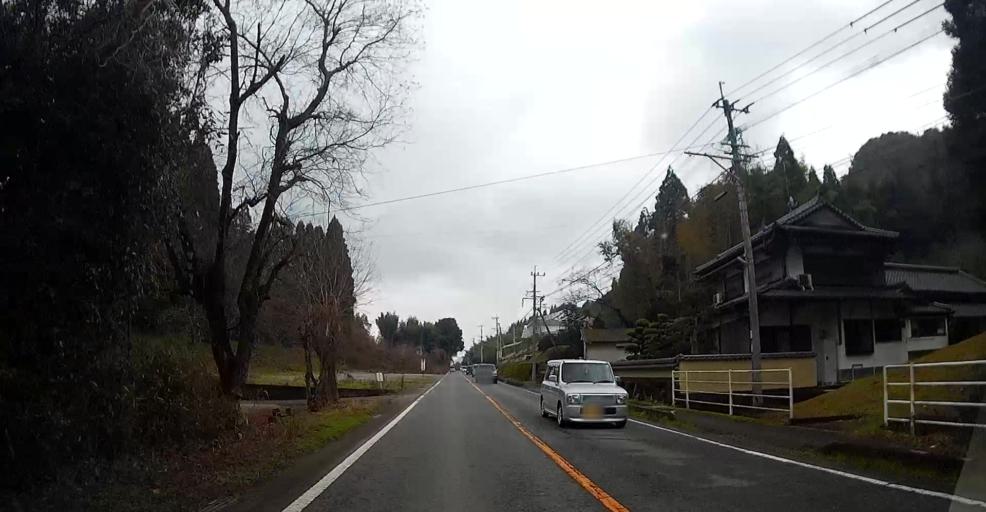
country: JP
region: Kumamoto
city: Matsubase
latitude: 32.6453
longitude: 130.7306
